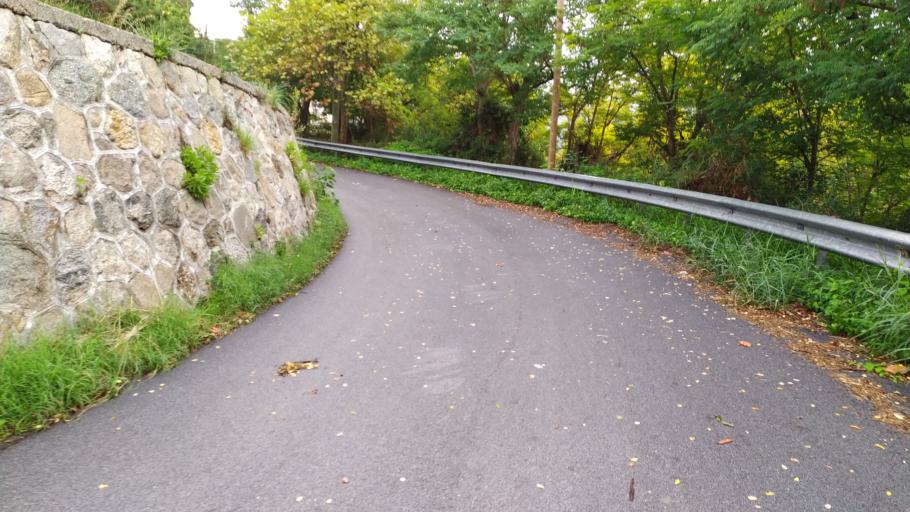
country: IT
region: Sicily
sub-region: Messina
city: Villafranca Tirrena
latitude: 38.2238
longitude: 15.4592
